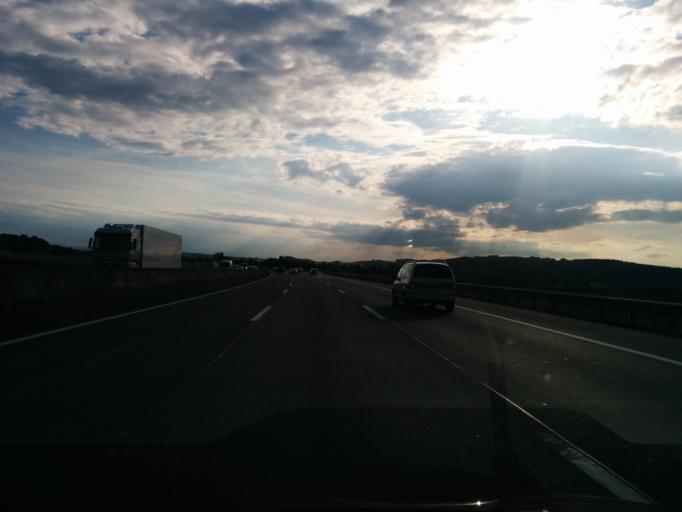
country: AT
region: Lower Austria
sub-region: Politischer Bezirk Melk
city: Pochlarn
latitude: 48.1913
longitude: 15.2008
